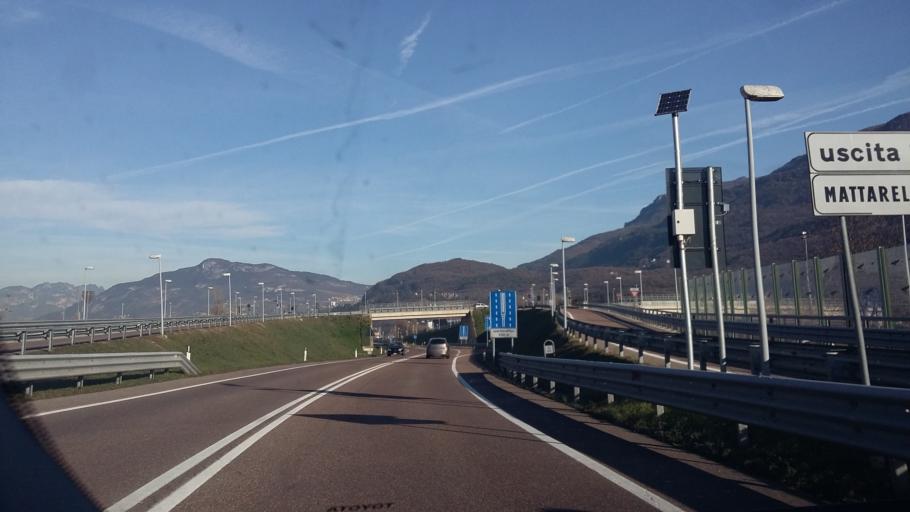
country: IT
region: Trentino-Alto Adige
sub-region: Provincia di Trento
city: Mattarello
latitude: 46.0078
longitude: 11.1239
